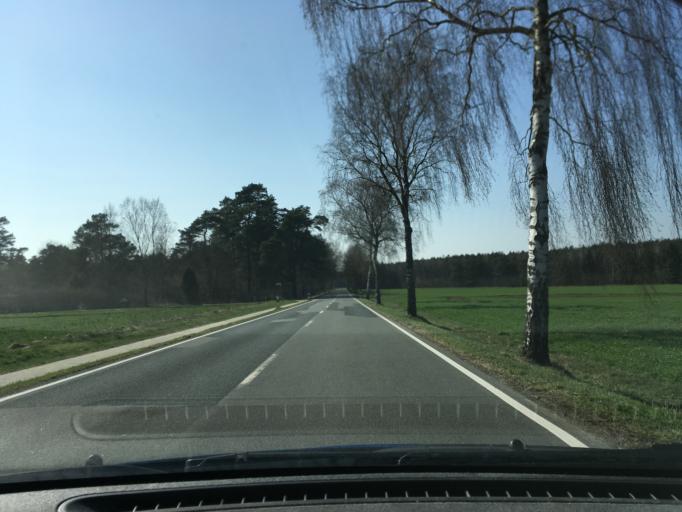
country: DE
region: Lower Saxony
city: Hermannsburg
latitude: 52.8234
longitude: 10.1382
